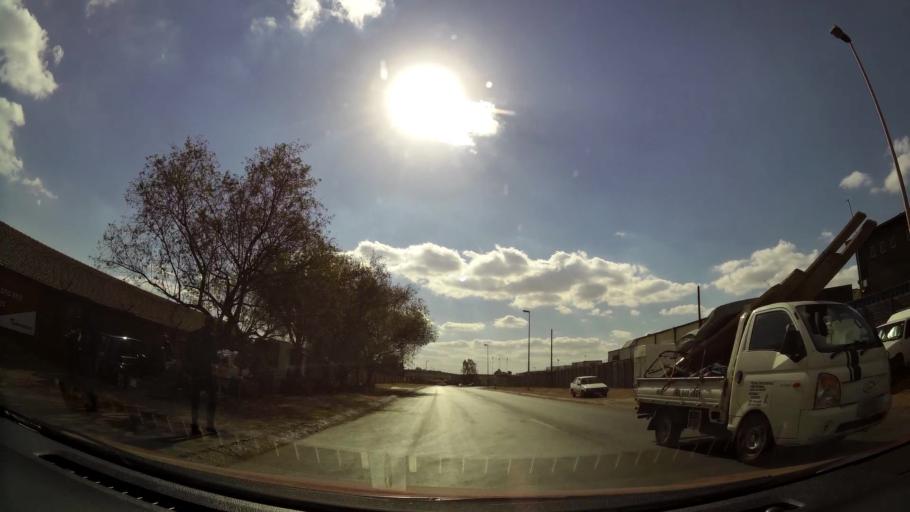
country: ZA
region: Gauteng
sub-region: Ekurhuleni Metropolitan Municipality
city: Tembisa
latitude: -25.9636
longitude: 28.2314
